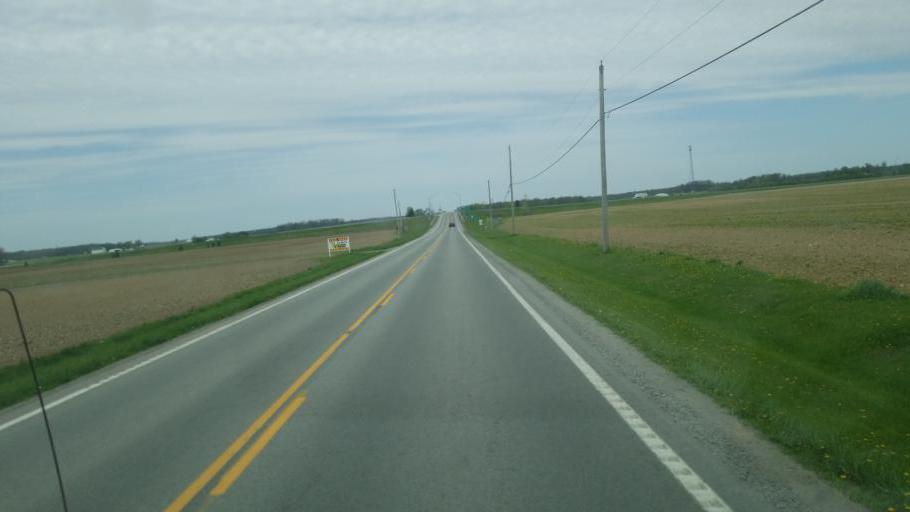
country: US
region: Ohio
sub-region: Hardin County
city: Ada
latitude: 40.8224
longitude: -83.8237
